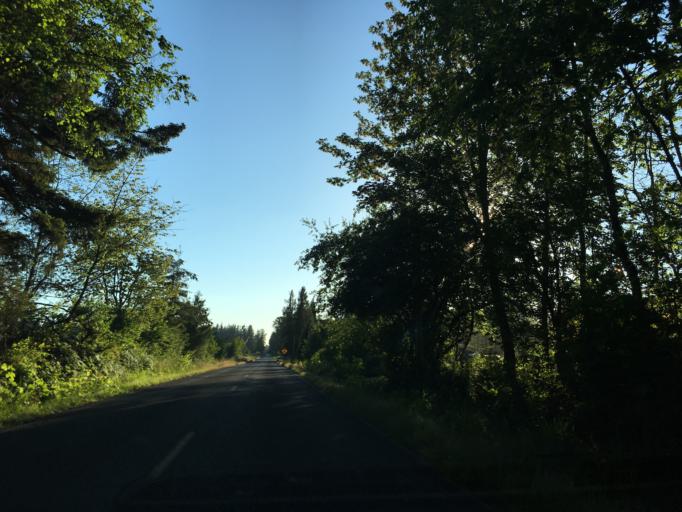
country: US
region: Washington
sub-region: Whatcom County
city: Geneva
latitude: 48.8184
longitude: -122.3739
